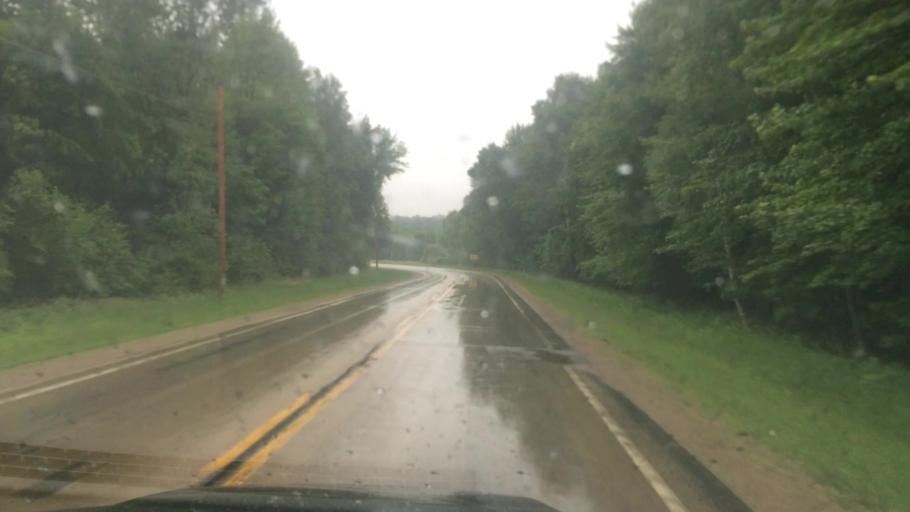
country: US
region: Wisconsin
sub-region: Waupaca County
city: Marion
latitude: 44.6143
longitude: -88.8725
